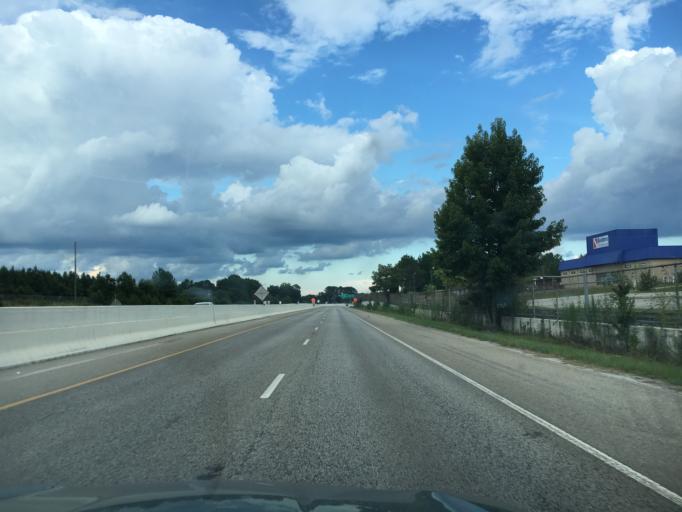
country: US
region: South Carolina
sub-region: Spartanburg County
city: Southern Shops
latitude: 34.9973
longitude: -81.9860
